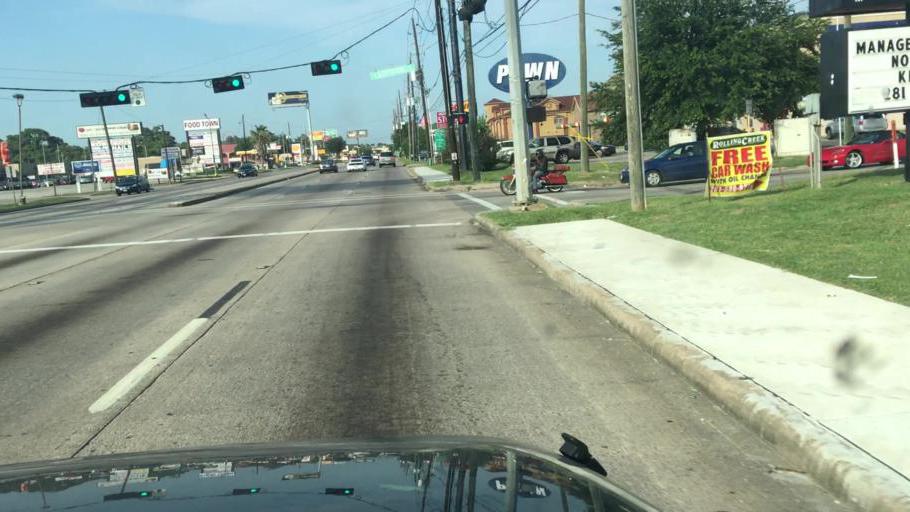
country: US
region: Texas
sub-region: Harris County
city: Spring
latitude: 30.0126
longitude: -95.4533
